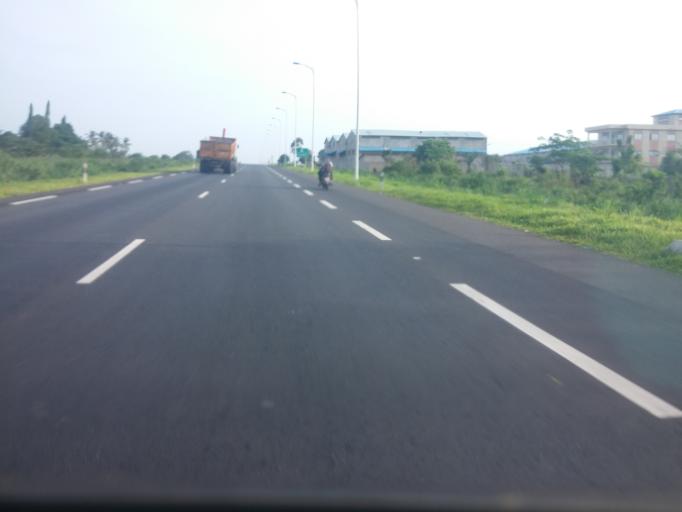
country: TG
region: Maritime
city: Tsevie
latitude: 6.3620
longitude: 1.2092
